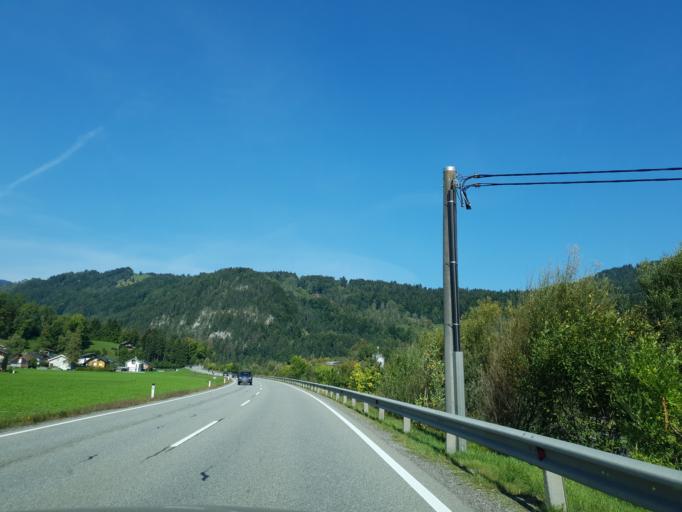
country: AT
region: Vorarlberg
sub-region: Politischer Bezirk Bregenz
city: Reuthe
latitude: 47.3805
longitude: 9.8875
